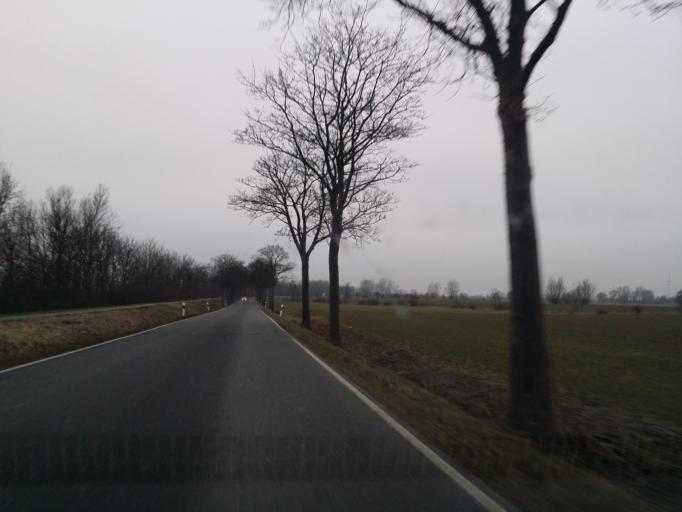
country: DE
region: Schleswig-Holstein
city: Fehmarn
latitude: 54.4580
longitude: 11.1302
